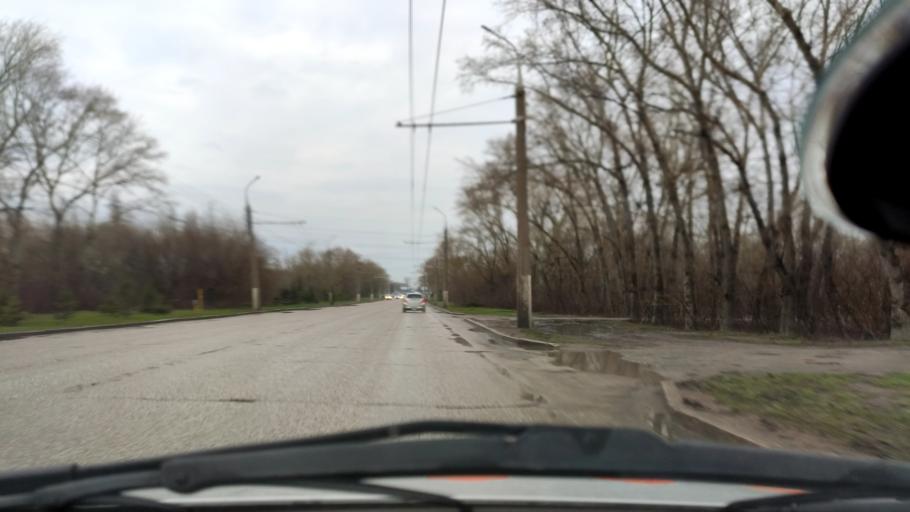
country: RU
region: Bashkortostan
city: Sterlitamak
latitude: 53.6588
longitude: 55.9488
